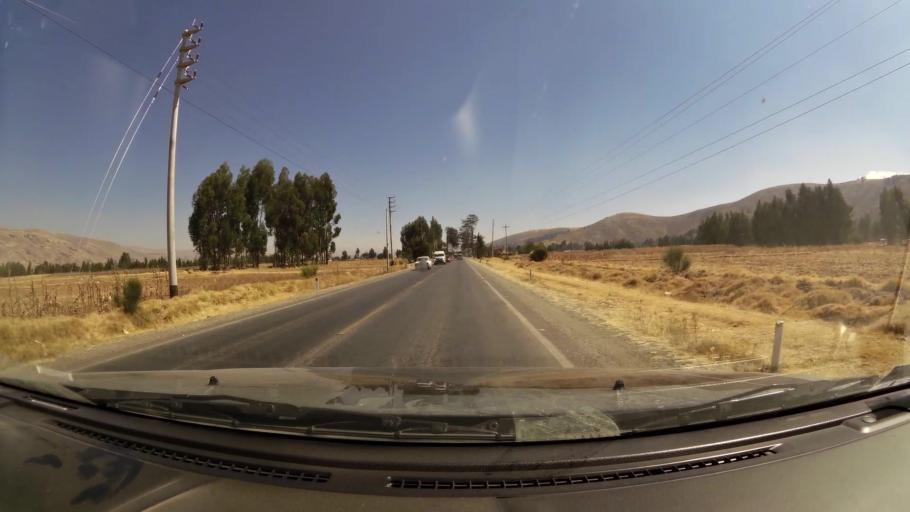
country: PE
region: Junin
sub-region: Provincia de Jauja
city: Huamali
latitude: -11.8169
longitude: -75.4199
